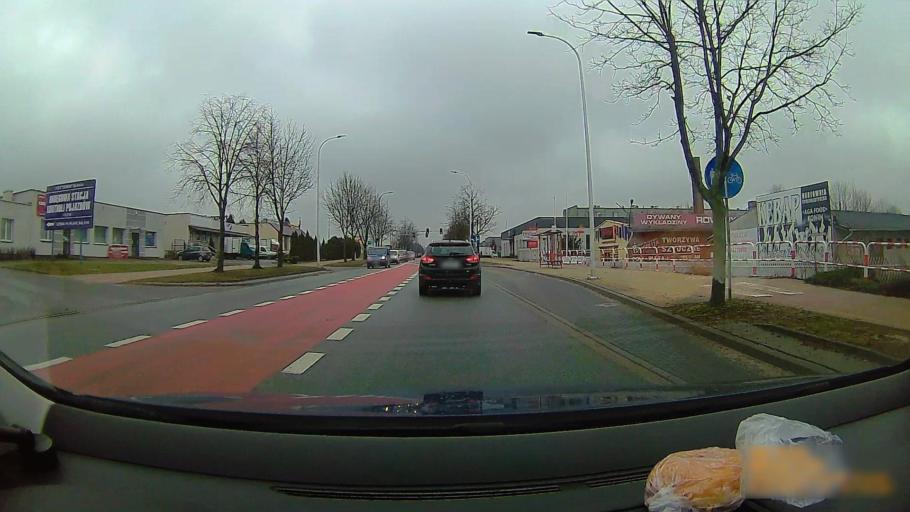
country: PL
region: Greater Poland Voivodeship
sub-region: Konin
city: Konin
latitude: 52.2315
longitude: 18.2335
